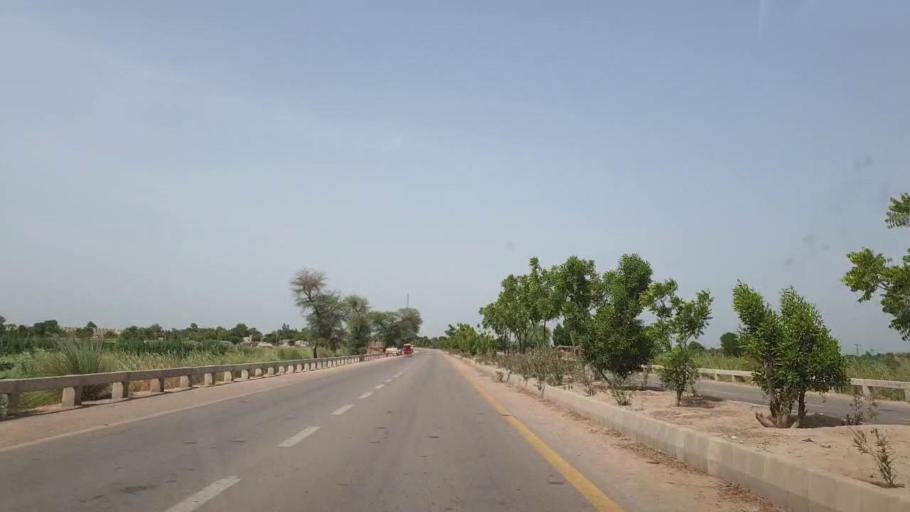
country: PK
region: Sindh
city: Sakrand
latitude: 26.1706
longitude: 68.2854
